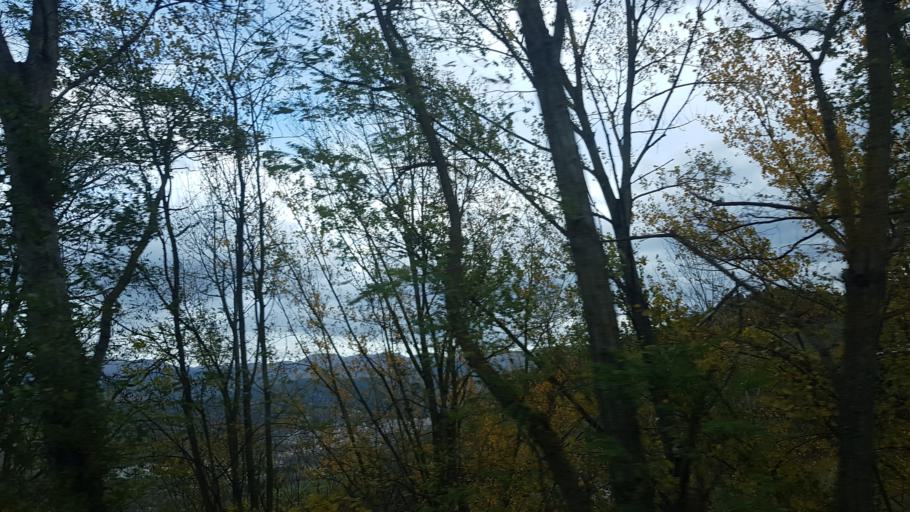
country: IT
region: Abruzzo
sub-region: Provincia dell' Aquila
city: Progetto Case Bazzano
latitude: 42.3589
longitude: 13.4298
